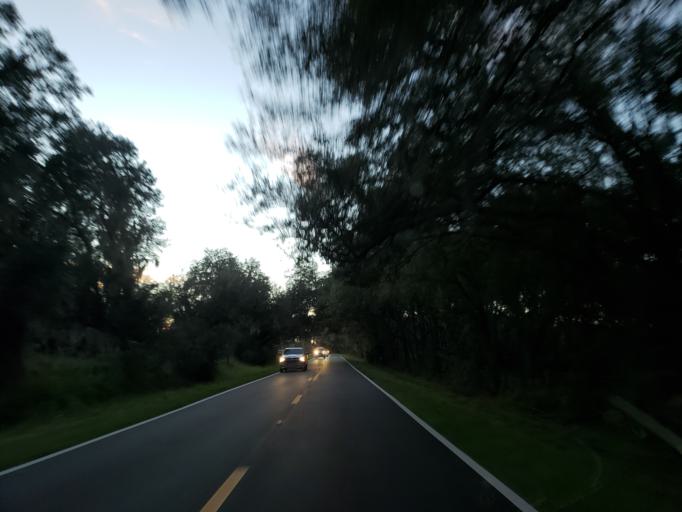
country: US
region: Florida
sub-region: Hillsborough County
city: Boyette
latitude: 27.8214
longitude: -82.2166
